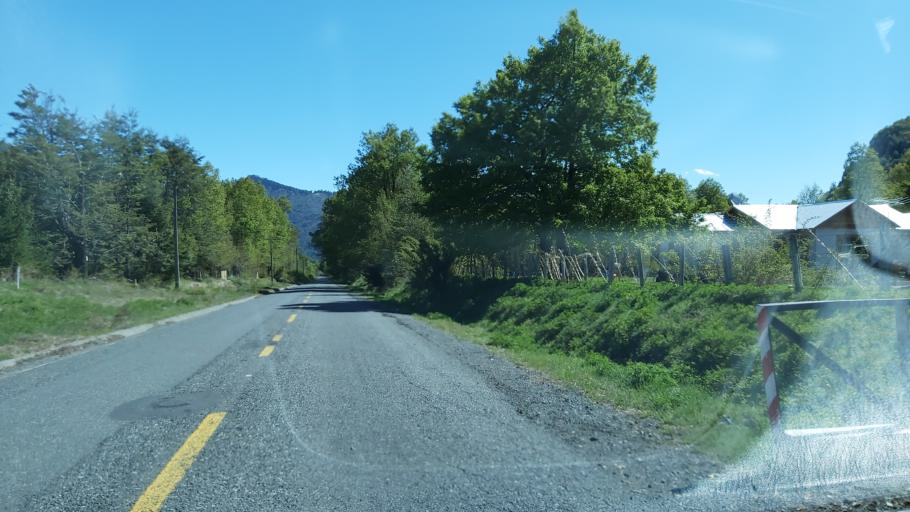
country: CL
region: Araucania
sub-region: Provincia de Cautin
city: Vilcun
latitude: -38.4687
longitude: -71.5224
